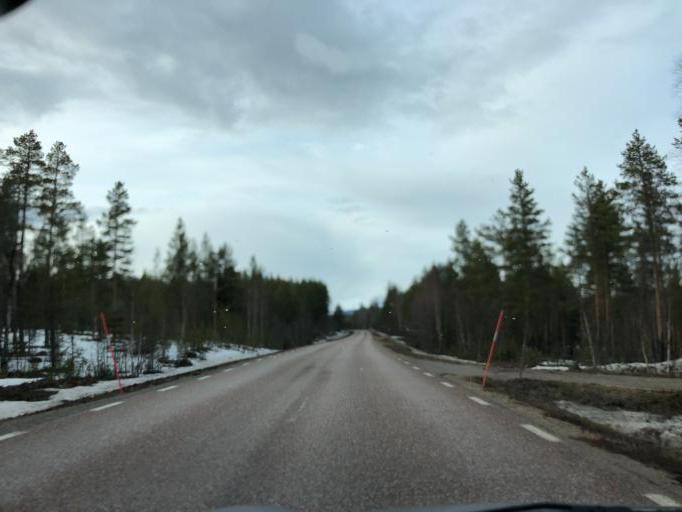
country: NO
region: Hedmark
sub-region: Trysil
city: Innbygda
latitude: 61.7519
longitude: 12.9616
